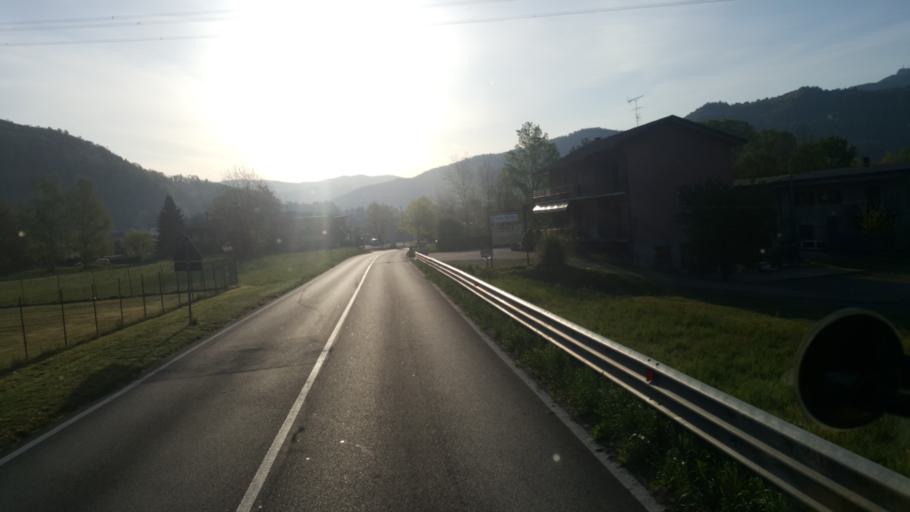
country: IT
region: Lombardy
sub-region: Provincia di Varese
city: Casalzuigno
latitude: 45.9068
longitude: 8.7189
